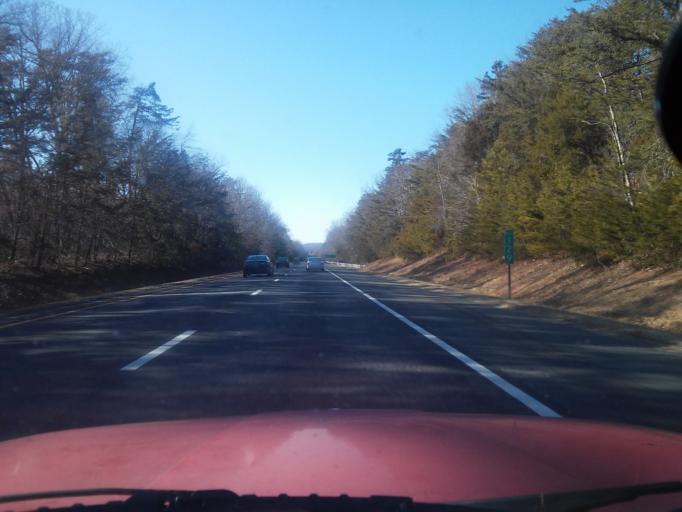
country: US
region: Virginia
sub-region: Fluvanna County
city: Lake Monticello
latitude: 38.0021
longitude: -78.3524
